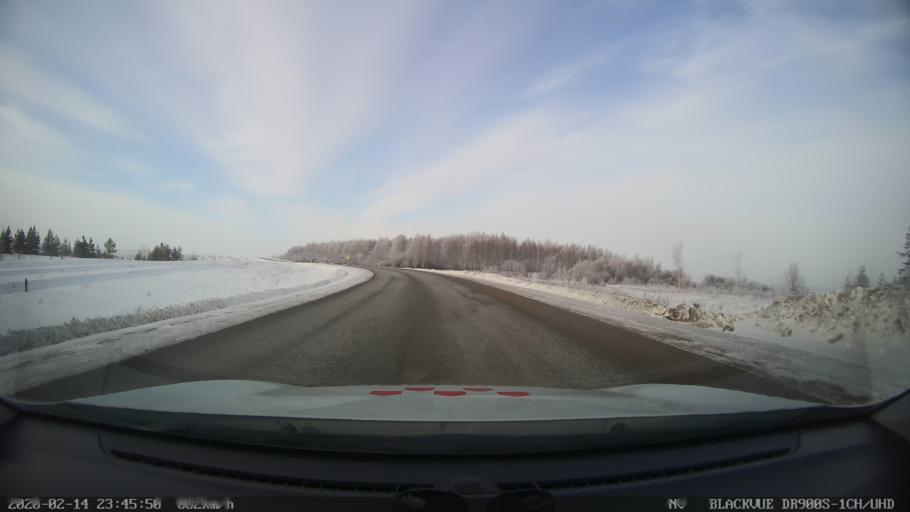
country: RU
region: Tatarstan
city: Kuybyshevskiy Zaton
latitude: 55.2254
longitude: 49.2330
